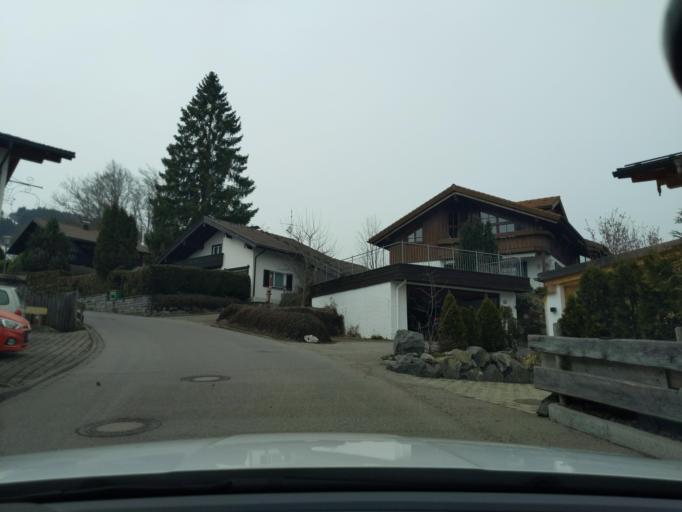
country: DE
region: Bavaria
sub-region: Swabia
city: Ofterschwang
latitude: 47.4957
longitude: 10.2401
